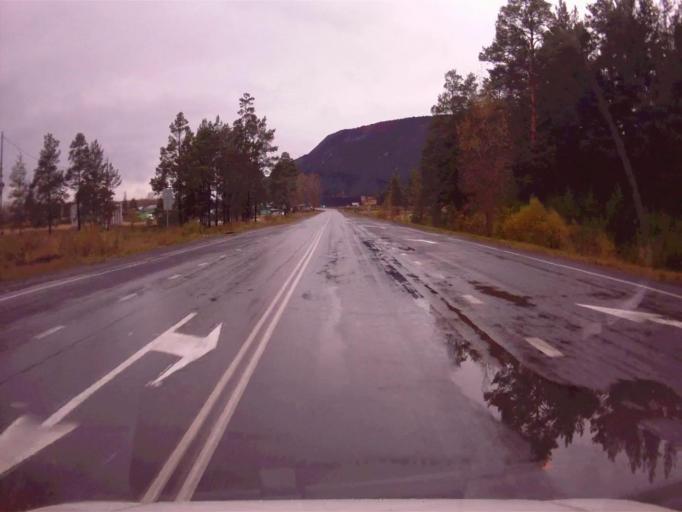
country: RU
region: Chelyabinsk
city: Verkhniy Ufaley
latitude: 56.0303
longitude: 60.2827
